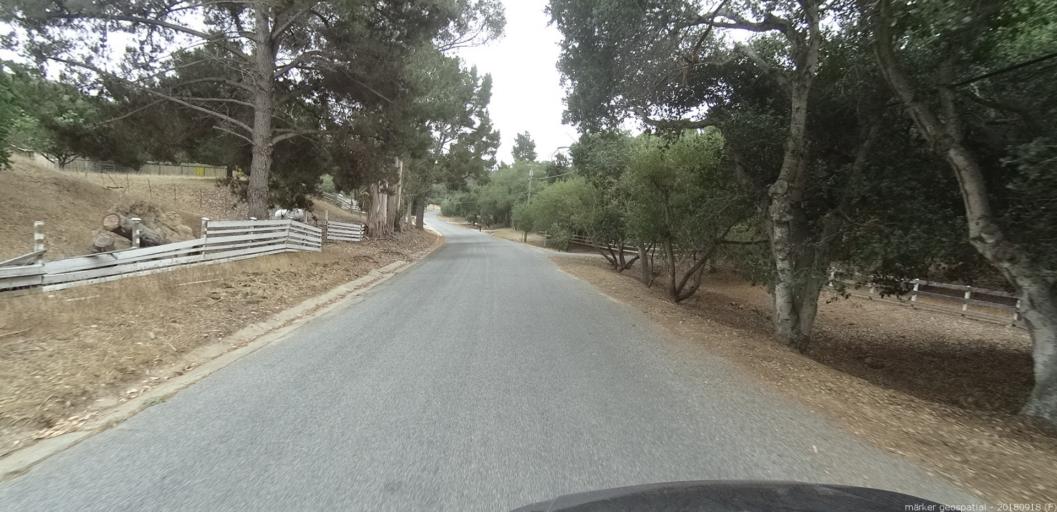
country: US
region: California
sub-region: Monterey County
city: Prunedale
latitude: 36.7868
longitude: -121.6419
